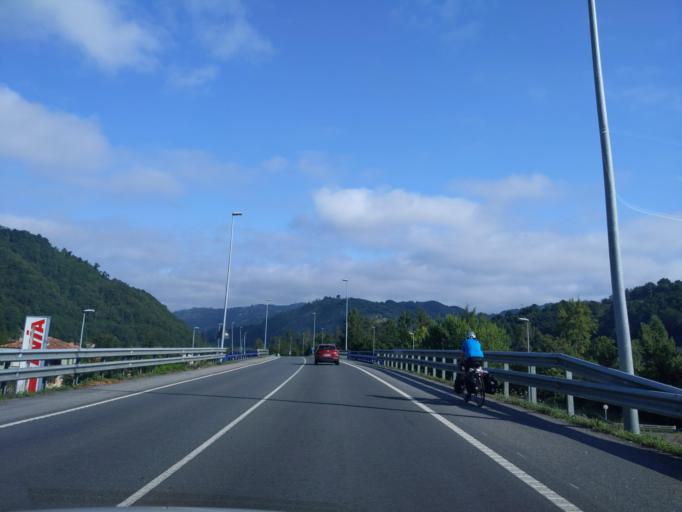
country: ES
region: Asturias
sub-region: Province of Asturias
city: Pola de Laviana
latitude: 43.2491
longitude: -5.5680
